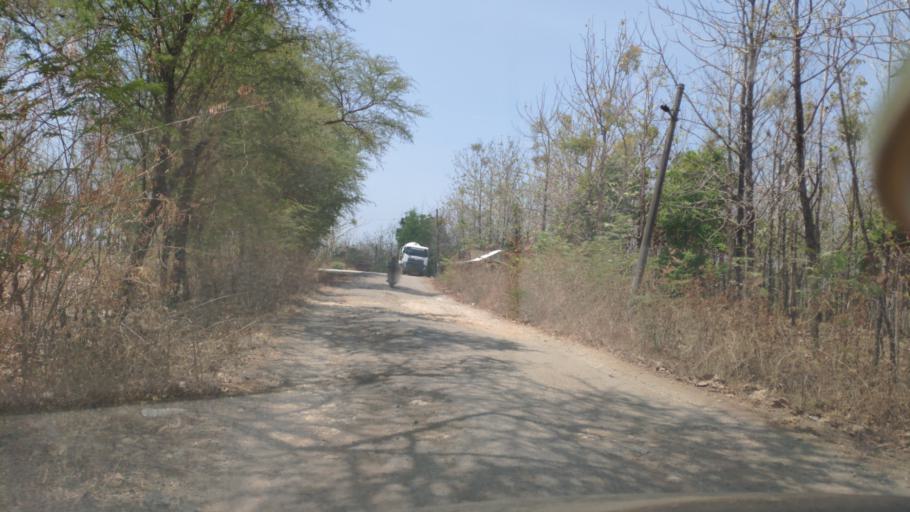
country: ID
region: Central Java
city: Randublatung
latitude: -7.2451
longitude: 111.3788
